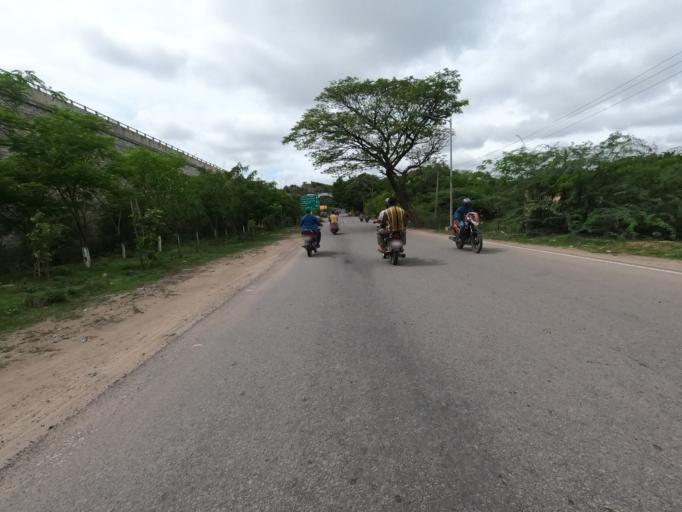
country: IN
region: Telangana
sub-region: Hyderabad
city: Hyderabad
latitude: 17.3250
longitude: 78.3742
